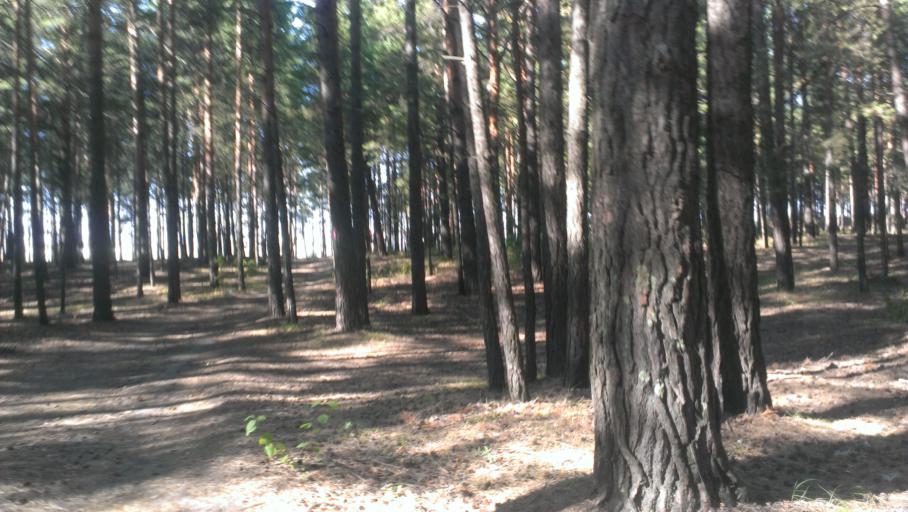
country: RU
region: Altai Krai
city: Novosilikatnyy
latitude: 53.3174
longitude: 83.6835
